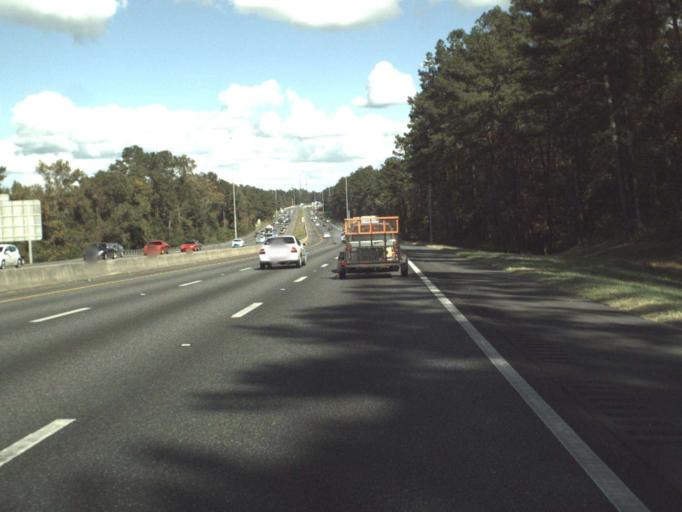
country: US
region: Florida
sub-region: Leon County
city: Tallahassee
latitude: 30.4937
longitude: -84.2757
